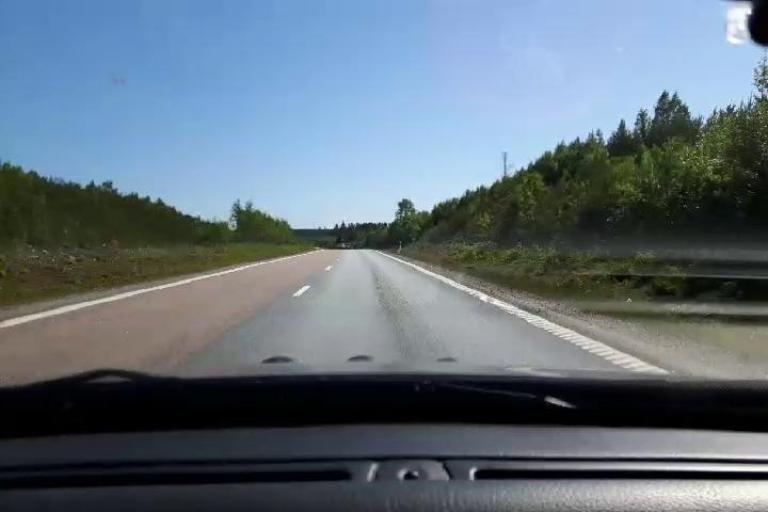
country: SE
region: Gaevleborg
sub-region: Hudiksvalls Kommun
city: Iggesund
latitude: 61.4922
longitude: 16.9837
